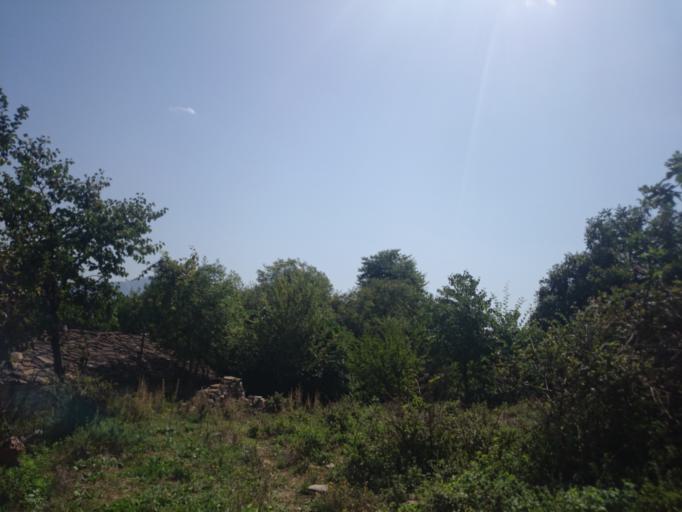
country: AL
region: Elbasan
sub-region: Rrethi i Gramshit
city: Kushove
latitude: 40.7490
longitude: 20.1666
